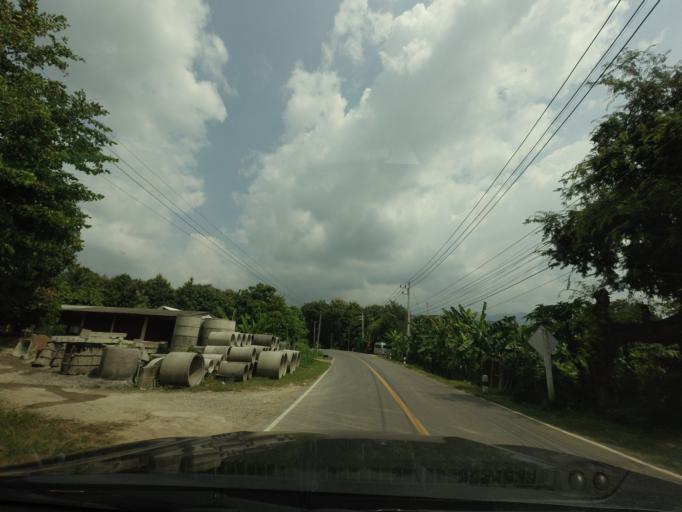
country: TH
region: Nan
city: Pua
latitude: 19.1793
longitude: 100.9455
